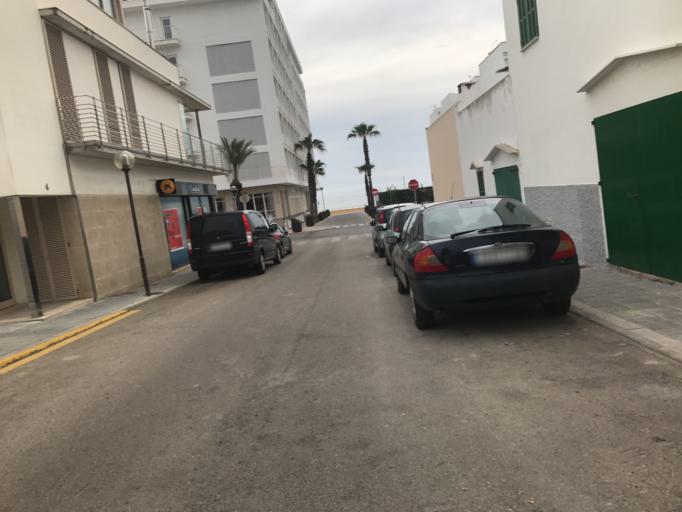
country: ES
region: Balearic Islands
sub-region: Illes Balears
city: Port d'Alcudia
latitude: 39.7655
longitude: 3.1553
